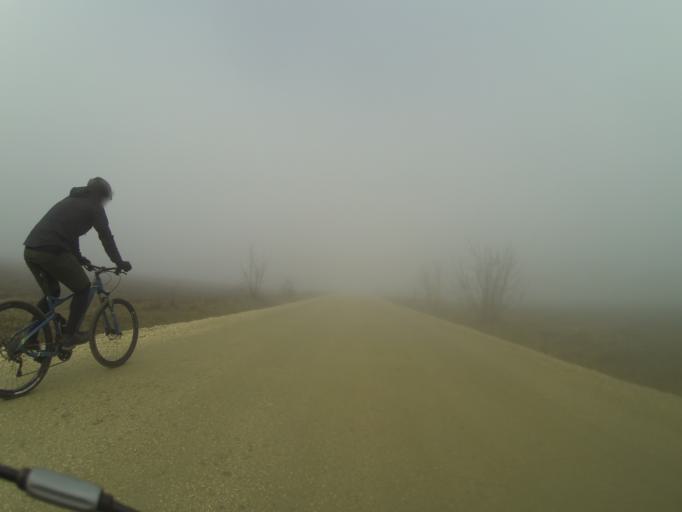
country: RO
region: Mehedinti
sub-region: Comuna Baclesu
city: Baclesu
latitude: 44.4454
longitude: 23.1278
